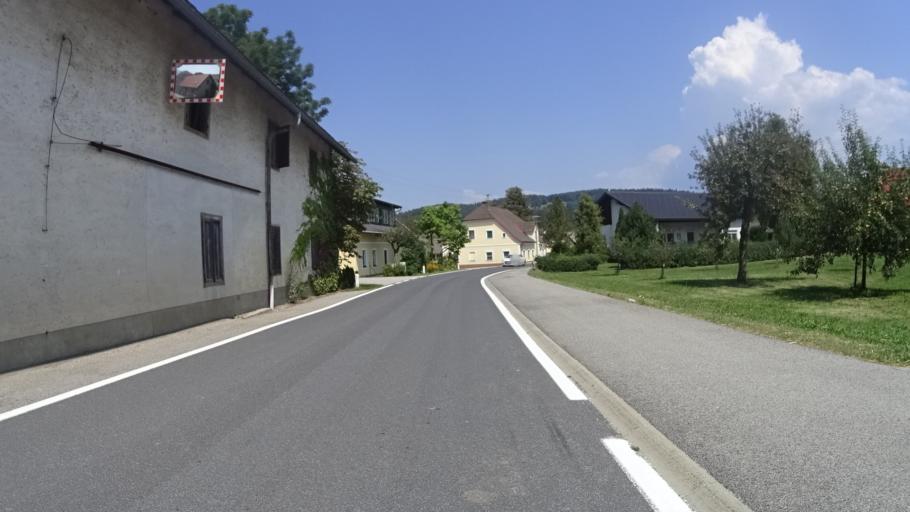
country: AT
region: Carinthia
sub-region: Politischer Bezirk Volkermarkt
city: Feistritz ob Bleiburg
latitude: 46.5735
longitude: 14.7708
